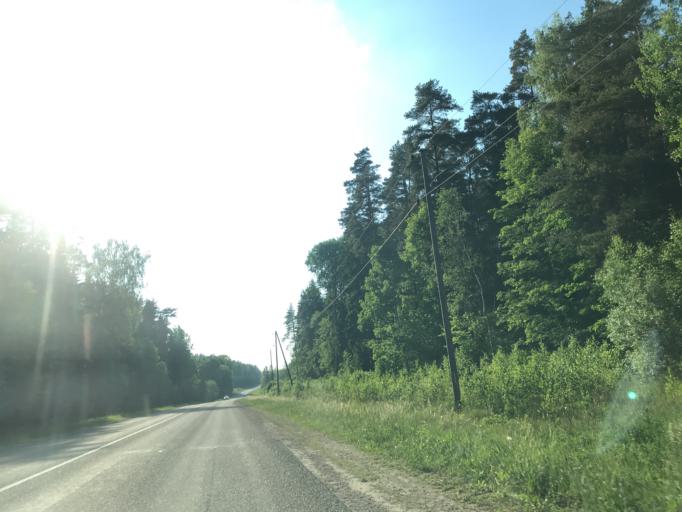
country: LV
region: Lielvarde
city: Lielvarde
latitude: 56.7035
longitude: 24.7943
